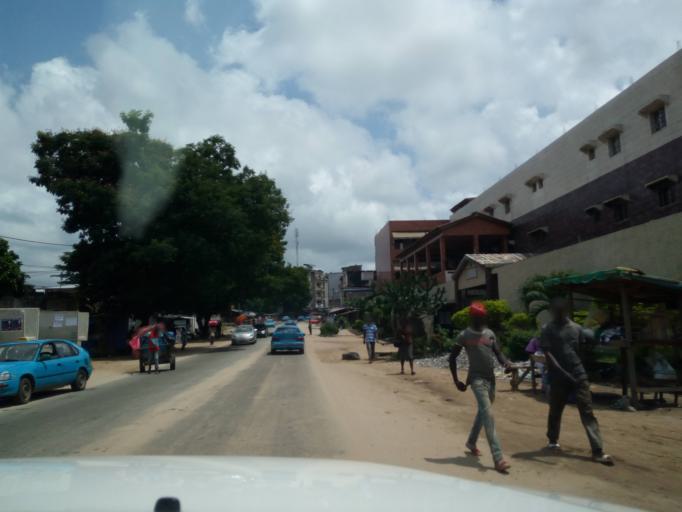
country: CI
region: Lagunes
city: Abidjan
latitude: 5.3395
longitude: -4.0953
